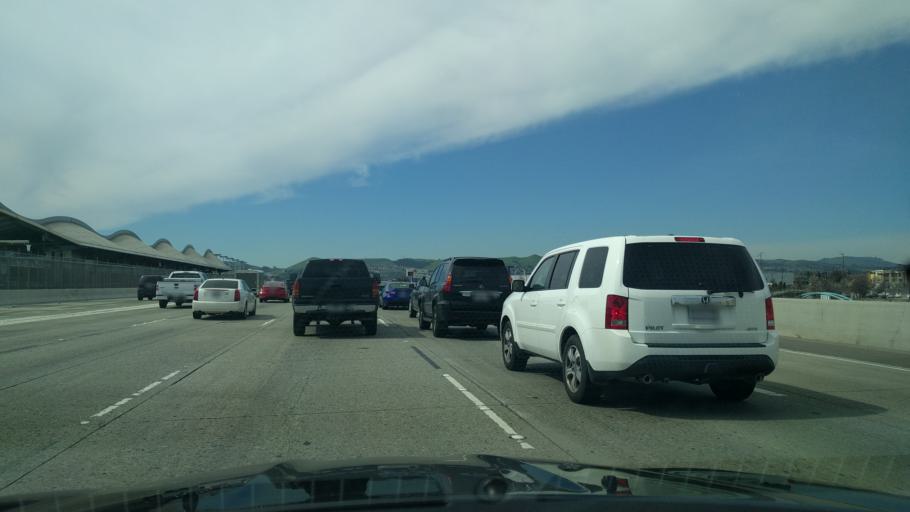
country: US
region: California
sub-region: Alameda County
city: Dublin
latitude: 37.7019
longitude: -121.8977
